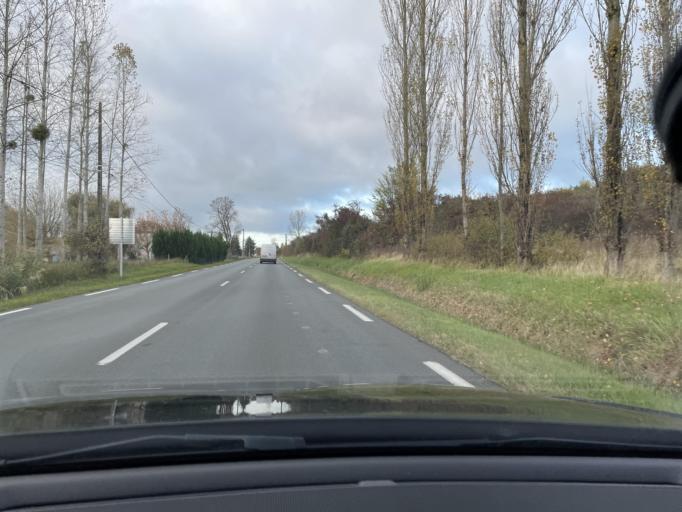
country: FR
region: Aquitaine
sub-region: Departement du Lot-et-Garonne
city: Casteljaloux
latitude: 44.3532
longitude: 0.1073
